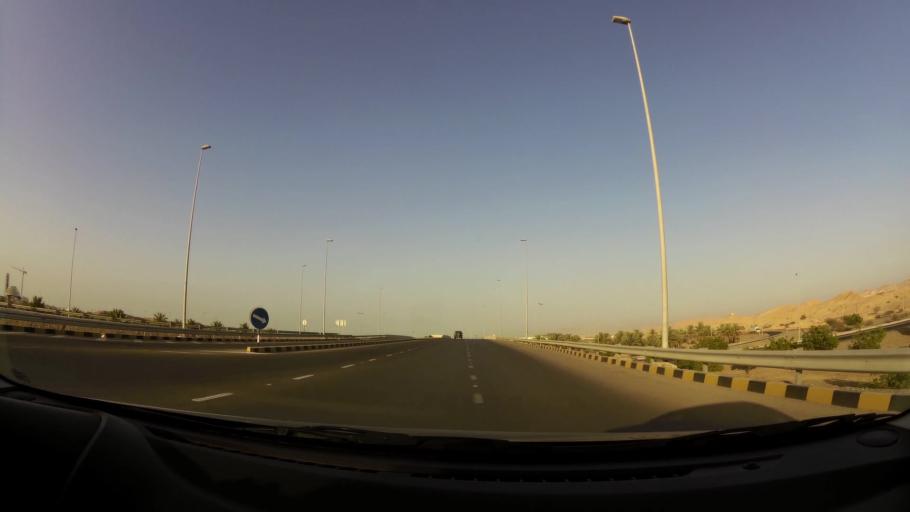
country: OM
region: Muhafazat Masqat
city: As Sib al Jadidah
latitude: 23.5731
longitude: 58.1910
